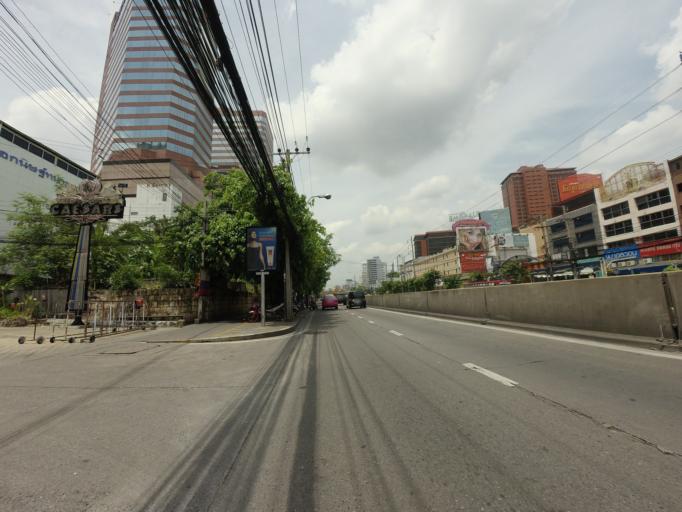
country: TH
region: Bangkok
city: Huai Khwang
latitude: 13.7773
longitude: 100.5737
